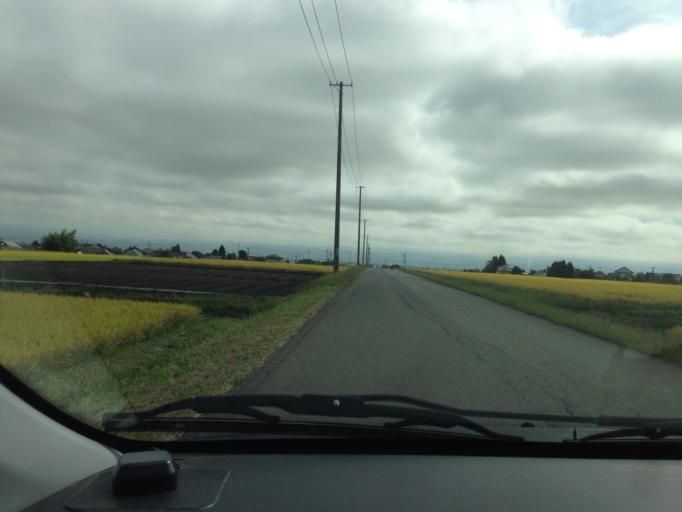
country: JP
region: Fukushima
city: Kitakata
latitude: 37.5234
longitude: 139.8152
